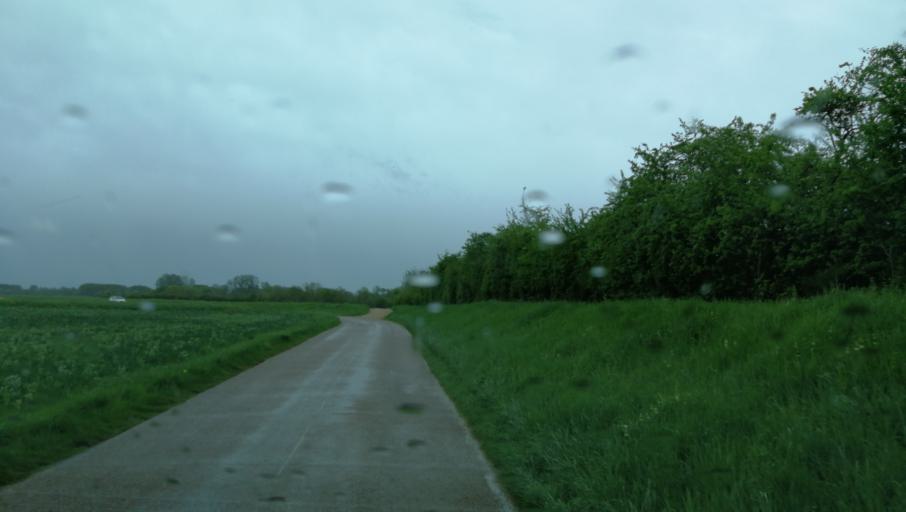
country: FR
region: Bourgogne
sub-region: Departement de Saone-et-Loire
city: Pierre-de-Bresse
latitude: 46.9328
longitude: 5.2248
